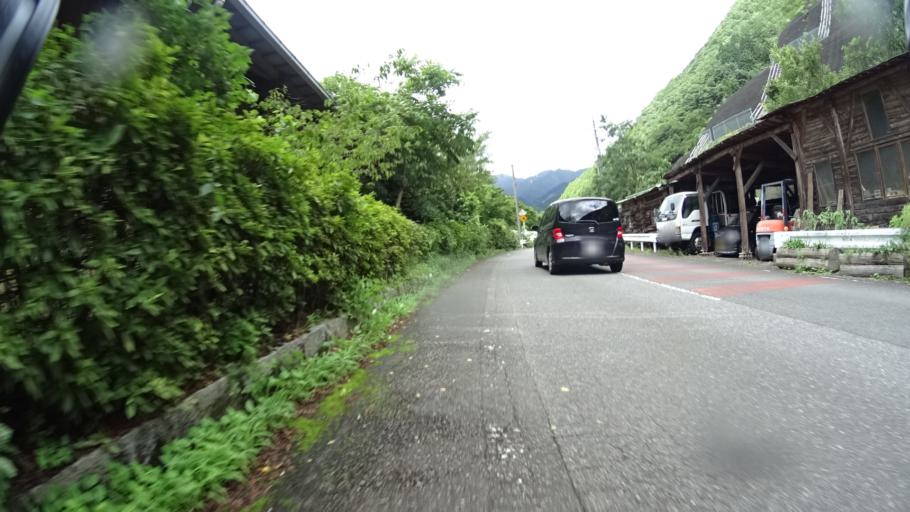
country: JP
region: Tokyo
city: Ome
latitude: 35.8752
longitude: 139.1675
